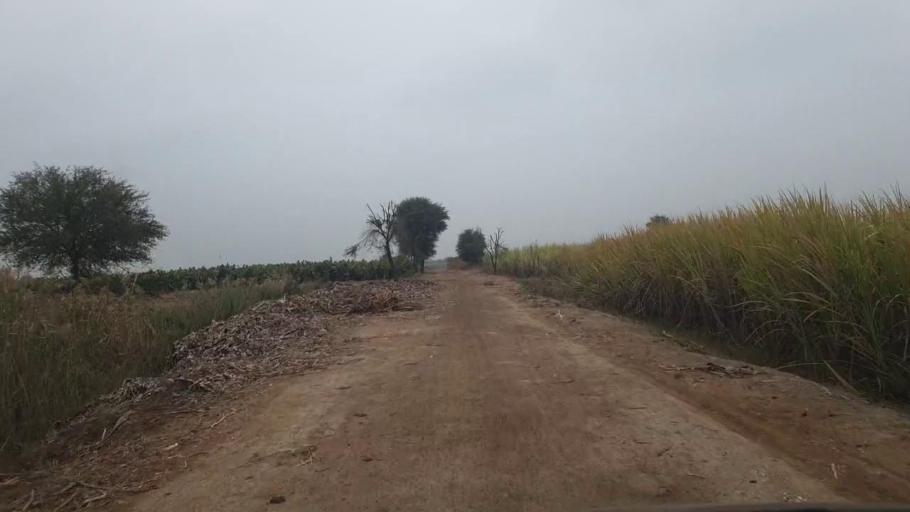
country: PK
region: Sindh
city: Tando Adam
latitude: 25.8323
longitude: 68.7226
